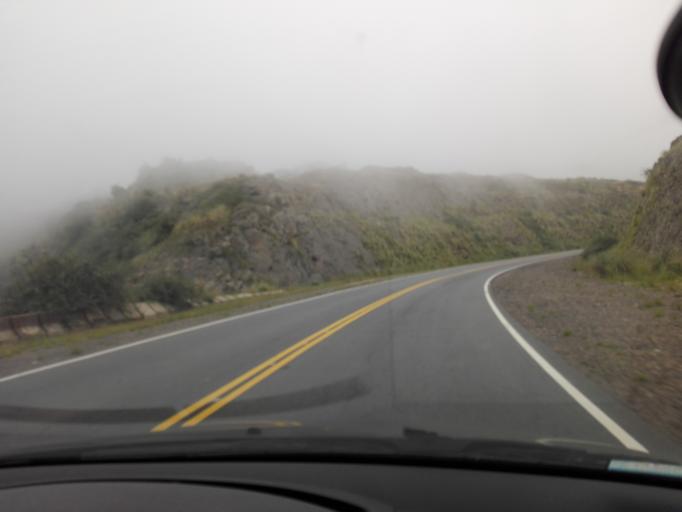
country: AR
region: Cordoba
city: Cuesta Blanca
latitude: -31.6053
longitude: -64.7004
